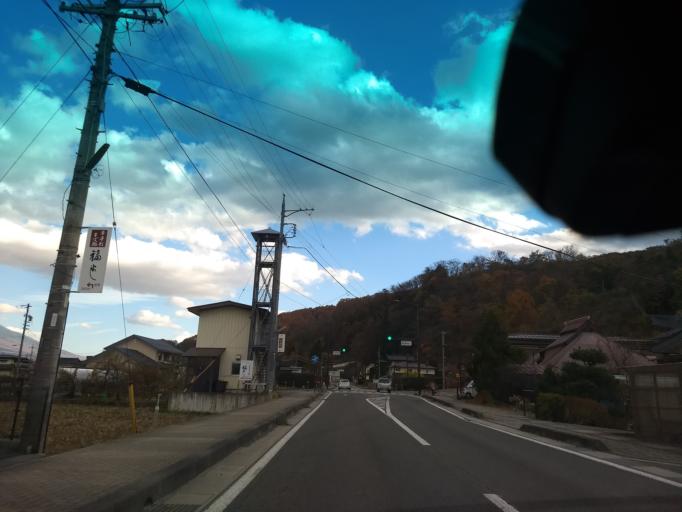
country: JP
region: Nagano
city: Chino
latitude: 35.9984
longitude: 138.1228
